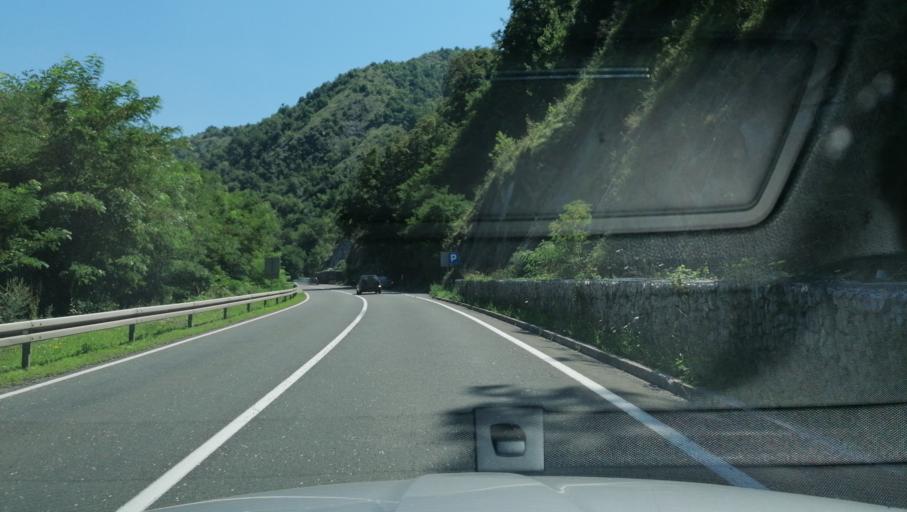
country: RS
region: Central Serbia
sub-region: Raski Okrug
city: Kraljevo
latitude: 43.5967
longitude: 20.5582
